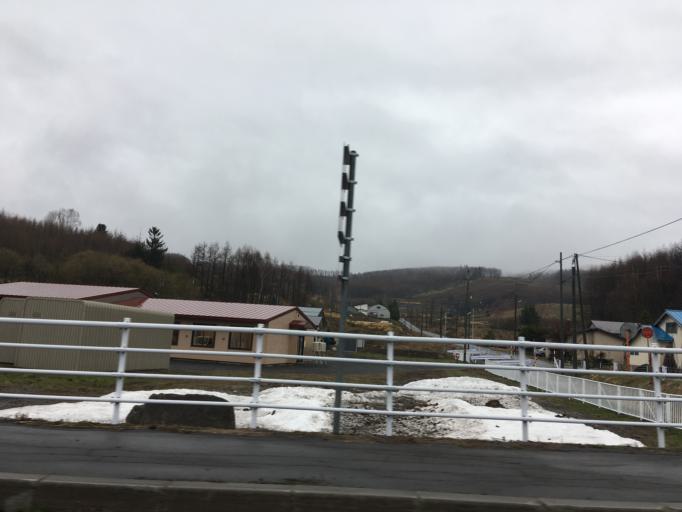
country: JP
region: Hokkaido
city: Nayoro
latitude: 44.0692
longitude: 142.4152
